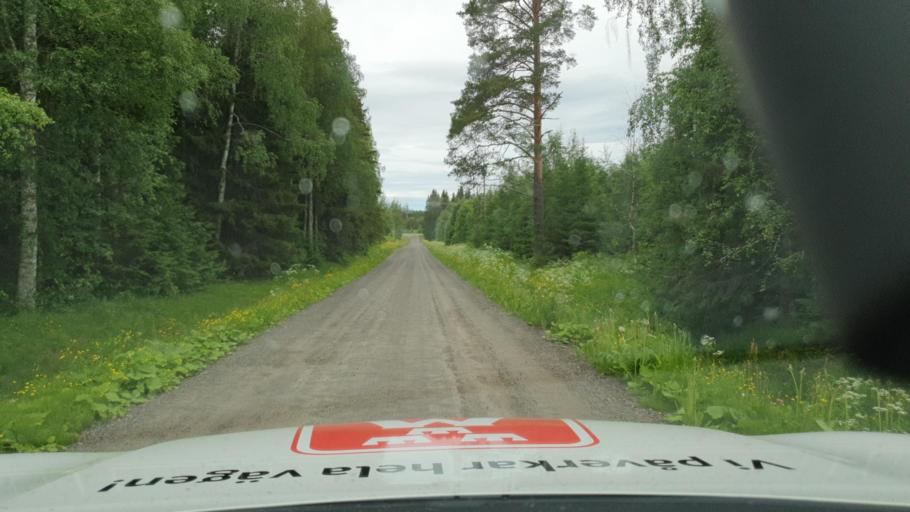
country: SE
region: Vaesterbotten
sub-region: Skelleftea Kommun
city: Burtraesk
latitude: 64.4014
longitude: 20.5552
